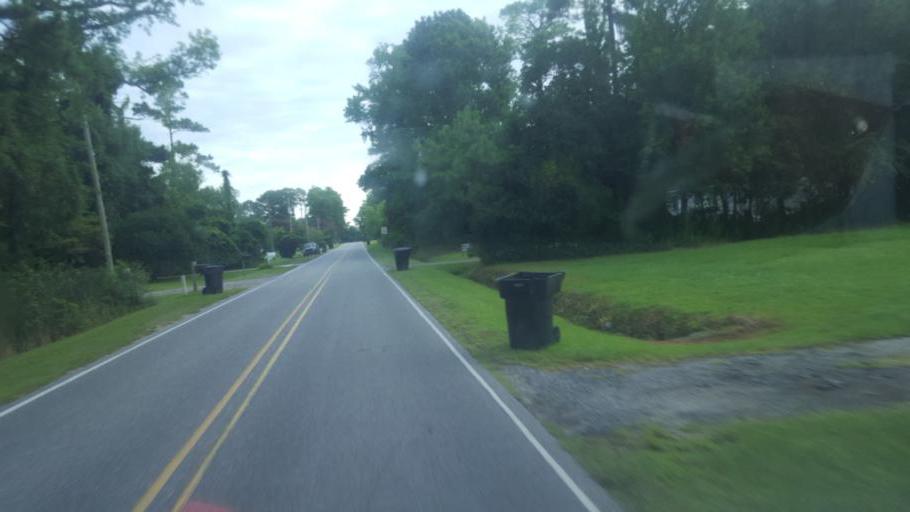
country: US
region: North Carolina
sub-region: Dare County
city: Wanchese
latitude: 35.8459
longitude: -75.6422
